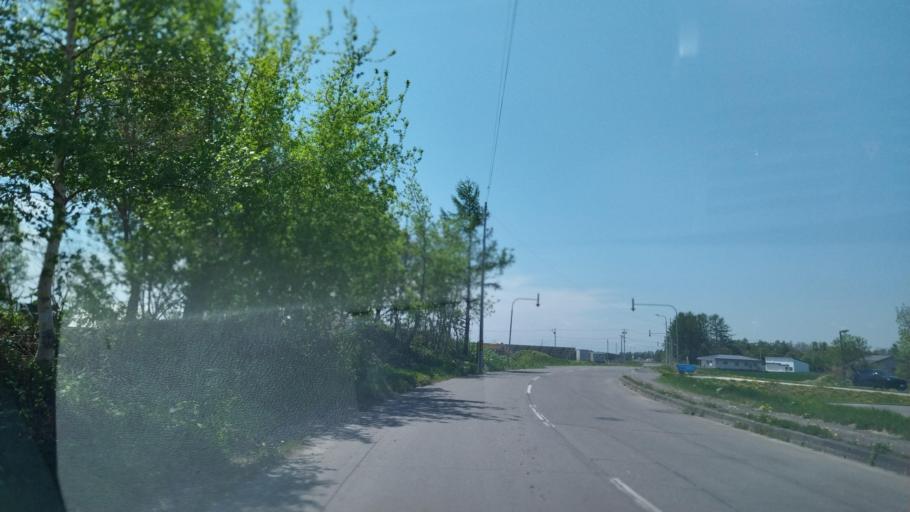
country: JP
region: Hokkaido
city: Otofuke
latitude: 43.2281
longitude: 143.2870
